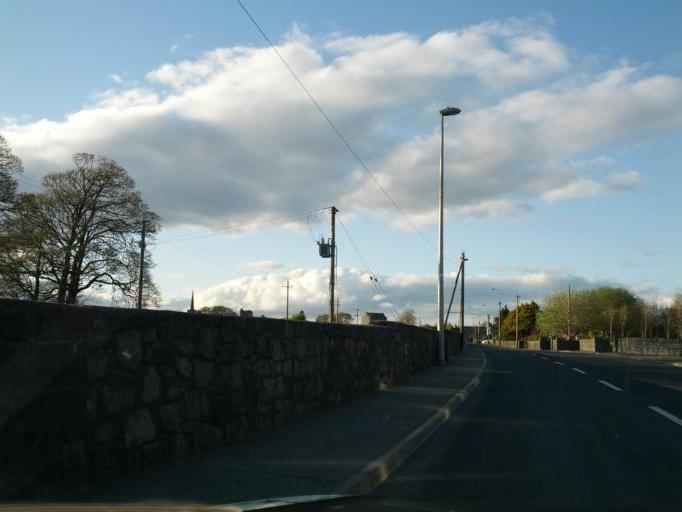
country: IE
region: Connaught
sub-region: County Galway
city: Athenry
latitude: 53.2958
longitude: -8.7423
